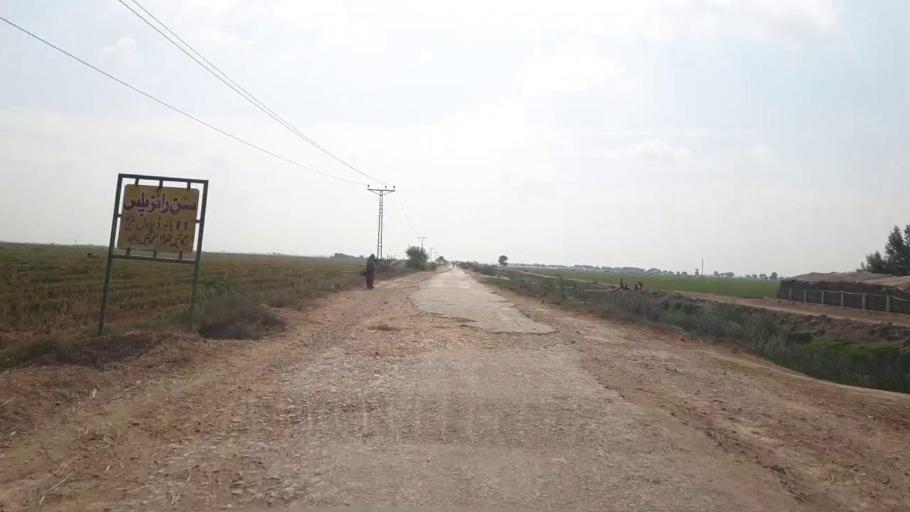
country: PK
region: Sindh
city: Kario
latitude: 24.6354
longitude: 68.5484
